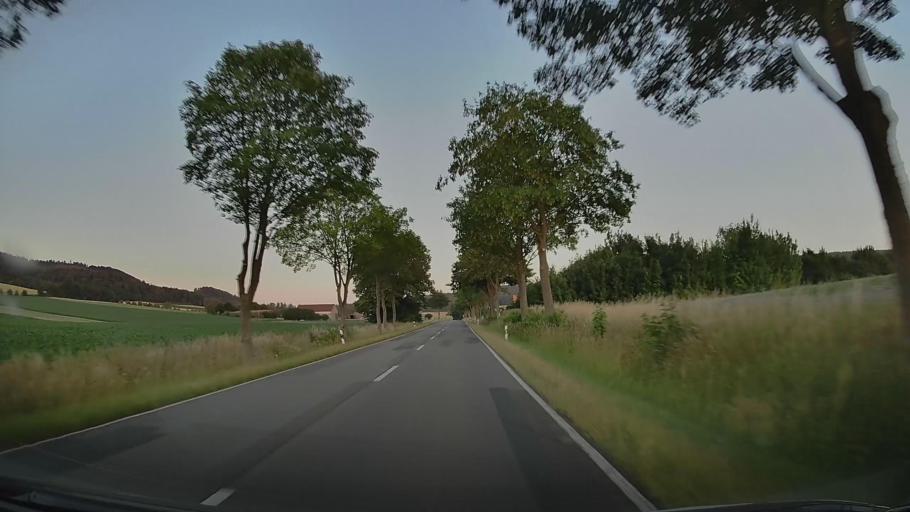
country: DE
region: Lower Saxony
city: Aerzen
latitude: 52.0368
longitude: 9.2644
